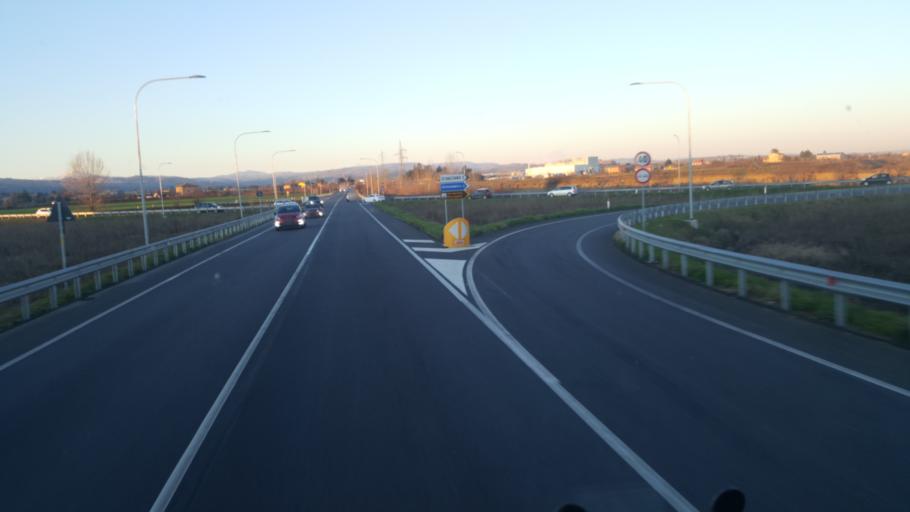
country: IT
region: Emilia-Romagna
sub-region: Provincia di Bologna
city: Bazzano
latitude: 44.5093
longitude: 11.0657
